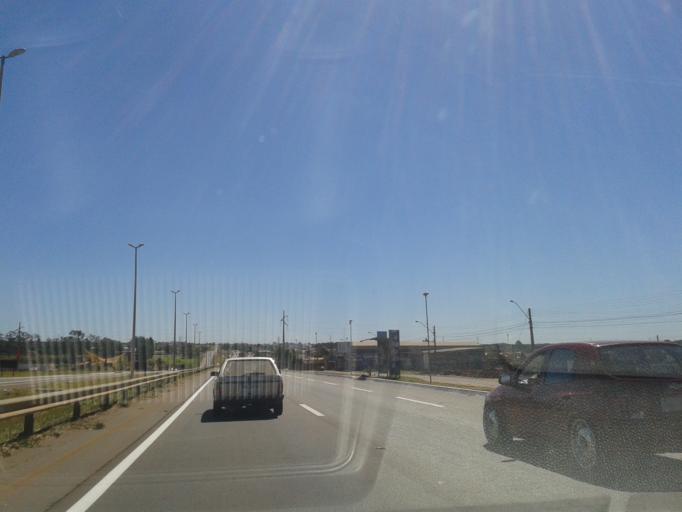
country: BR
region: Goias
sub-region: Goianira
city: Goianira
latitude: -16.5759
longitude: -49.3909
